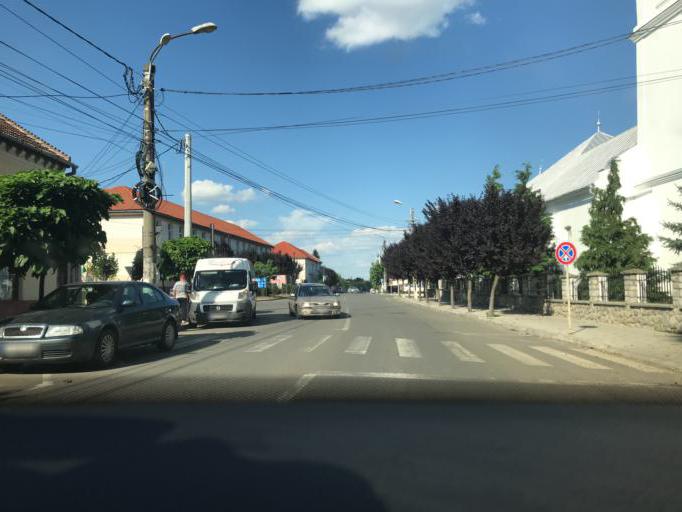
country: RO
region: Bihor
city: Margita
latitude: 47.3469
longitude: 22.3413
